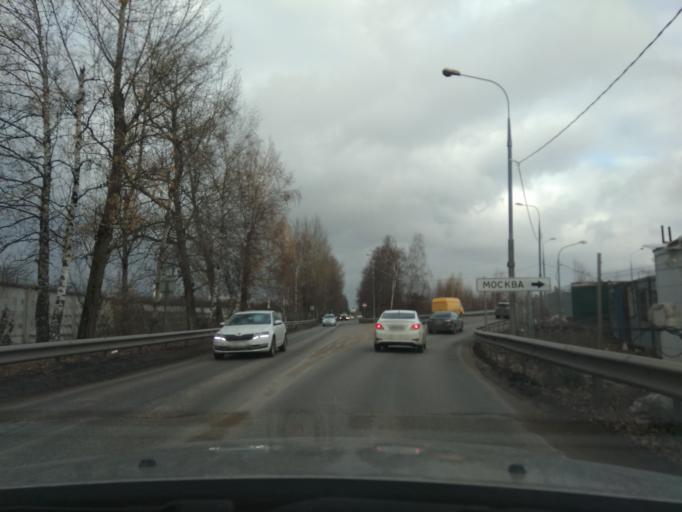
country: RU
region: Moscow
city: Biryulevo
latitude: 55.5684
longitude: 37.6895
